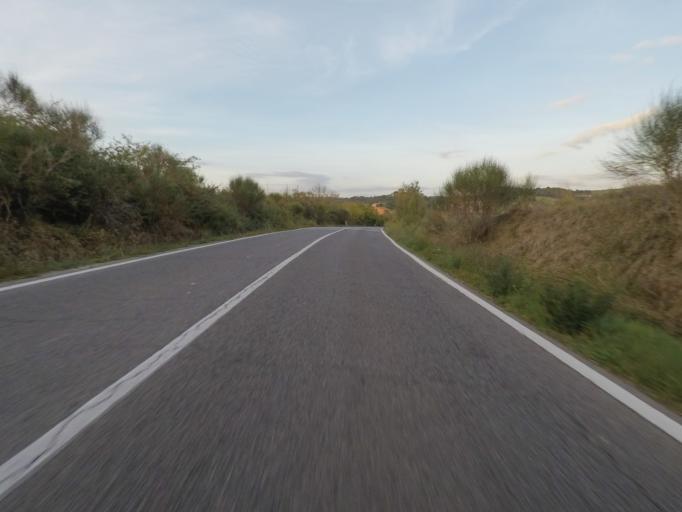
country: IT
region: Tuscany
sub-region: Provincia di Siena
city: Pienza
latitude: 43.0946
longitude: 11.6892
